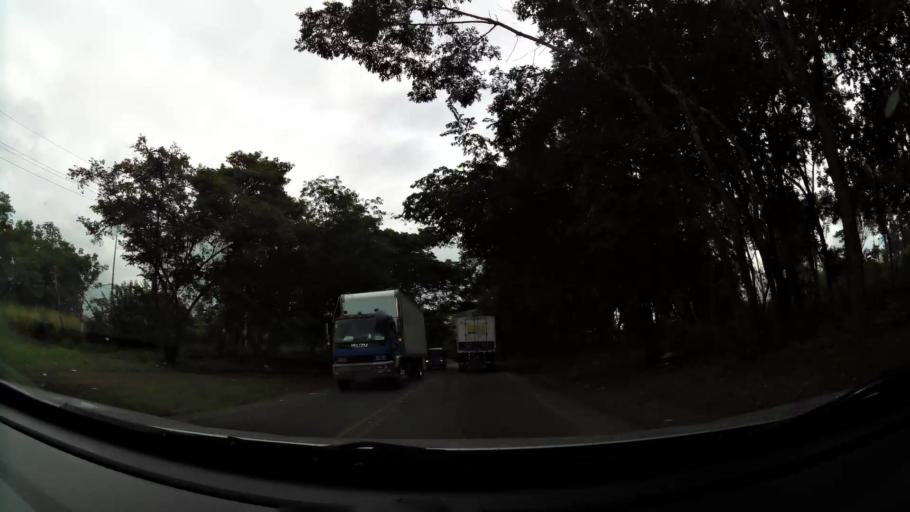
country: CR
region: Guanacaste
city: Juntas
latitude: 10.1682
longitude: -84.9210
